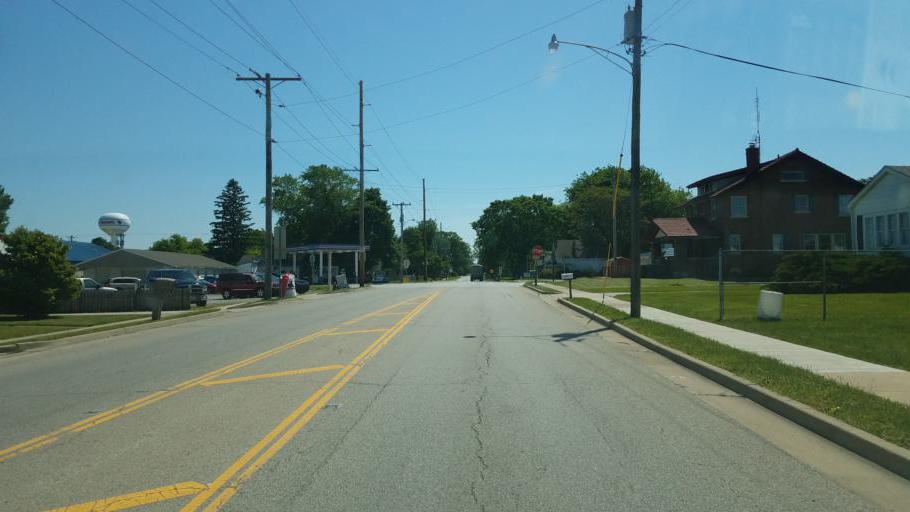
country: US
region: Illinois
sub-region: McLean County
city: Heyworth
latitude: 40.3120
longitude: -88.9810
